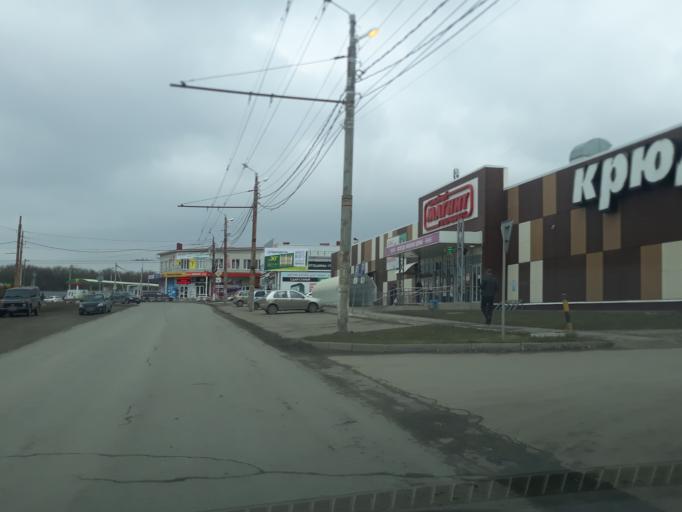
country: RU
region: Rostov
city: Taganrog
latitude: 47.2785
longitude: 38.9246
